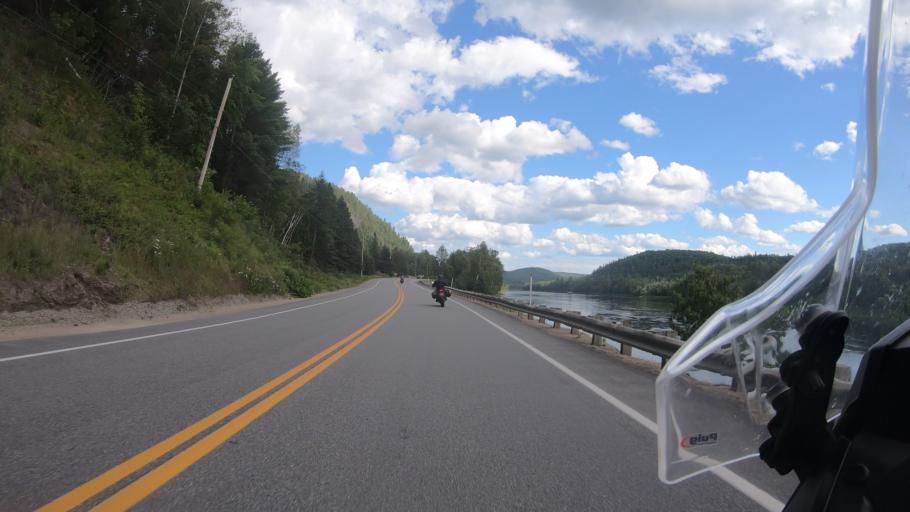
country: CA
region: Quebec
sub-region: Mauricie
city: Saint-Tite
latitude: 46.9938
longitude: -72.9165
